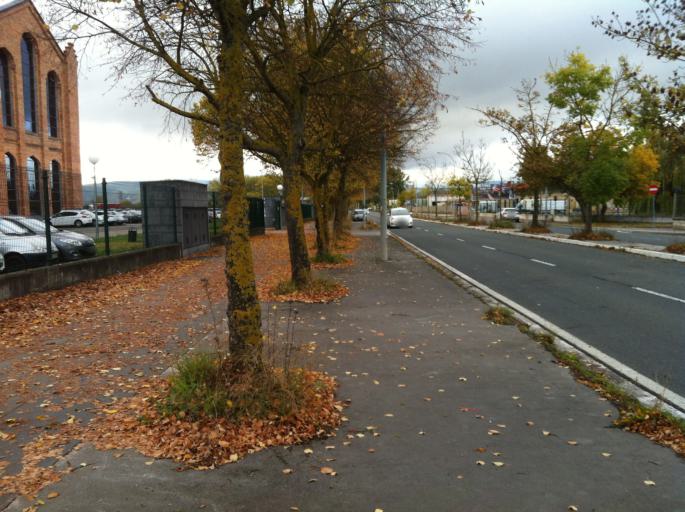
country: ES
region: Basque Country
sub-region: Provincia de Alava
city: Gasteiz / Vitoria
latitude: 42.8572
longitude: -2.7182
